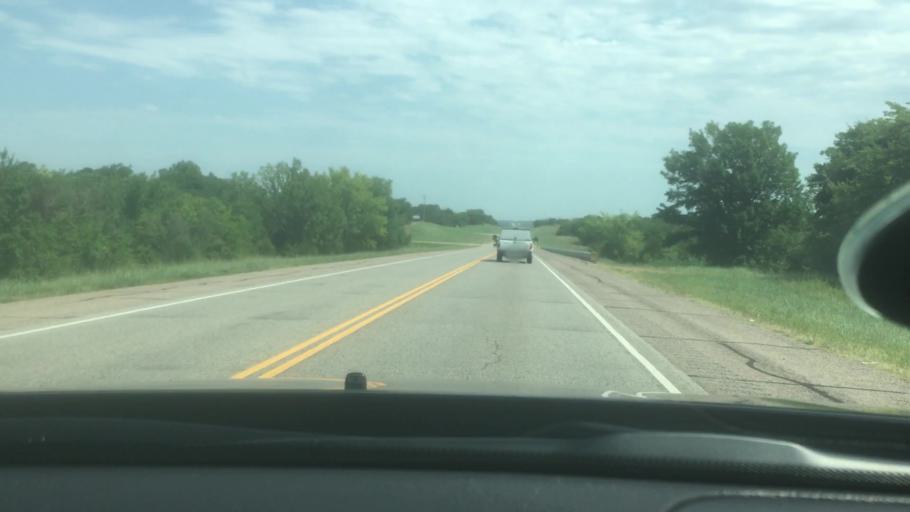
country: US
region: Oklahoma
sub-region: Seminole County
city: Maud
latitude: 35.0488
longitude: -96.9315
